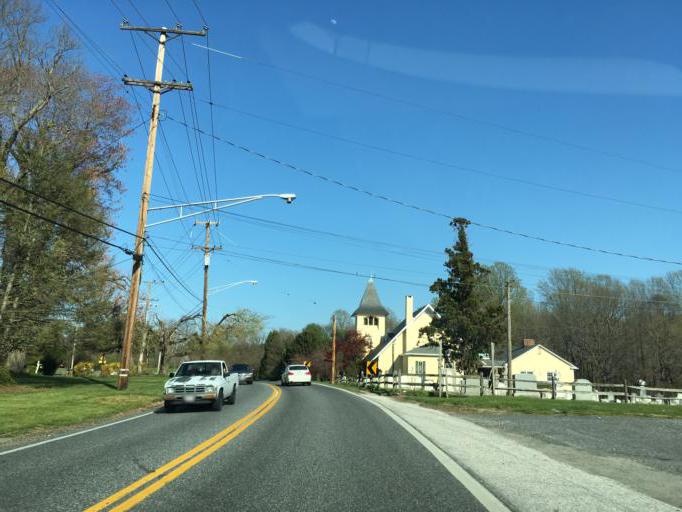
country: US
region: Maryland
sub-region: Baltimore County
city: Hunt Valley
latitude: 39.5131
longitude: -76.5511
